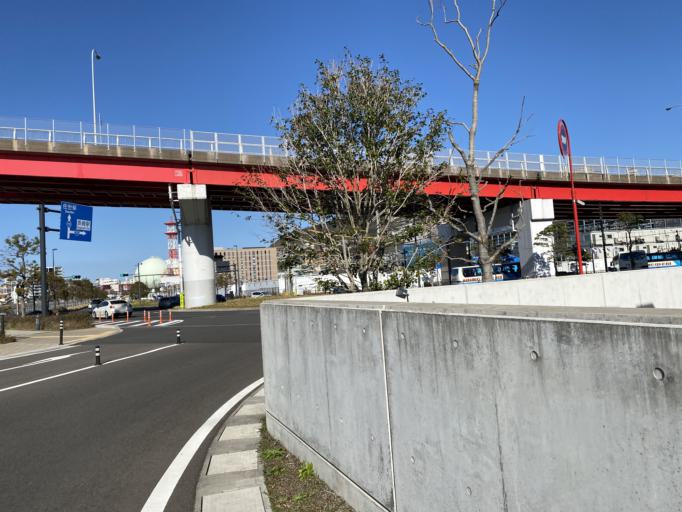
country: JP
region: Nagasaki
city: Nagasaki-shi
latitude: 32.7508
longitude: 129.8669
